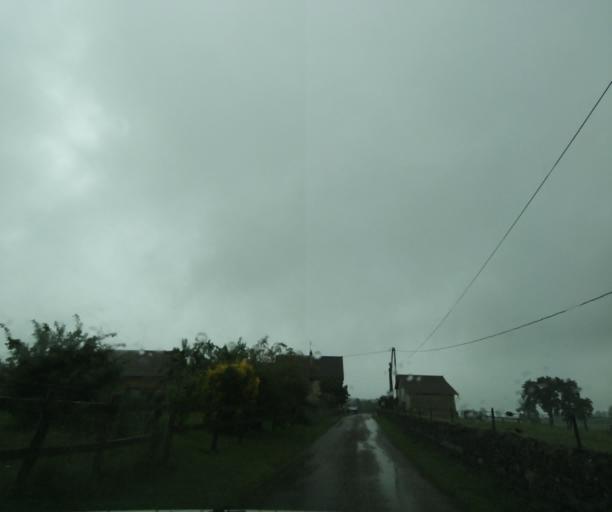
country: FR
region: Bourgogne
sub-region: Departement de Saone-et-Loire
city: La Clayette
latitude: 46.3466
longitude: 4.2336
